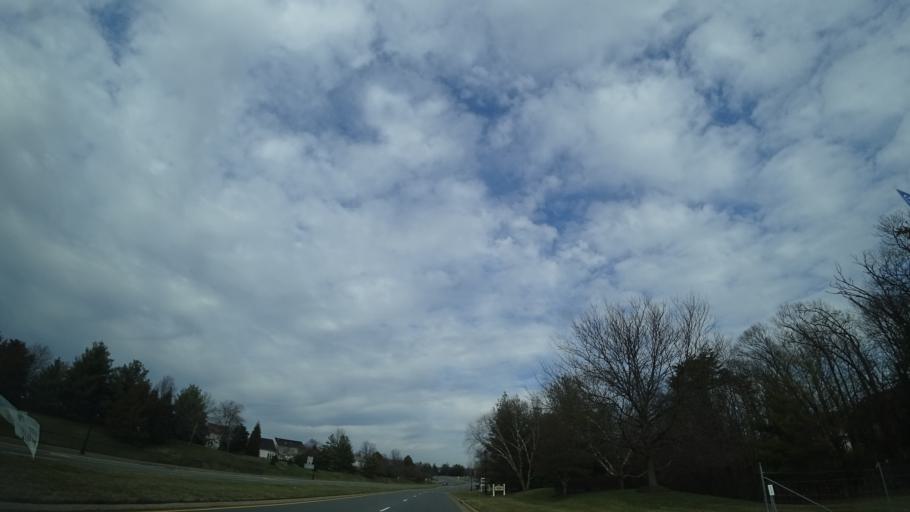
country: US
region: Virginia
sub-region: Loudoun County
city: Broadlands
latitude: 39.0313
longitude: -77.5072
